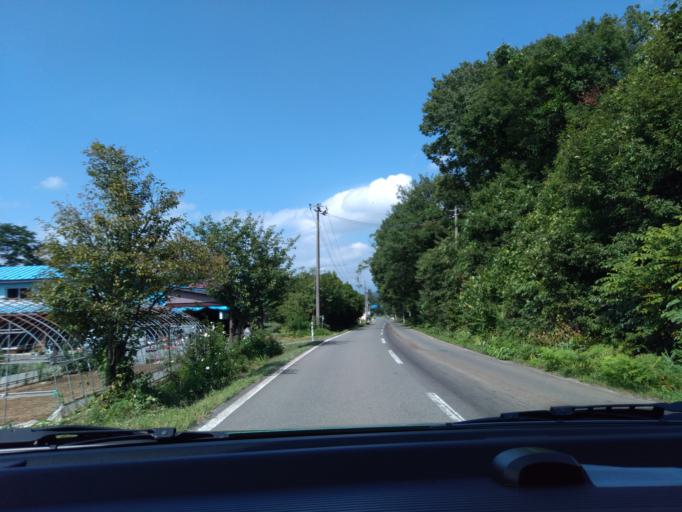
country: JP
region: Iwate
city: Shizukuishi
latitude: 39.6563
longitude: 140.9922
